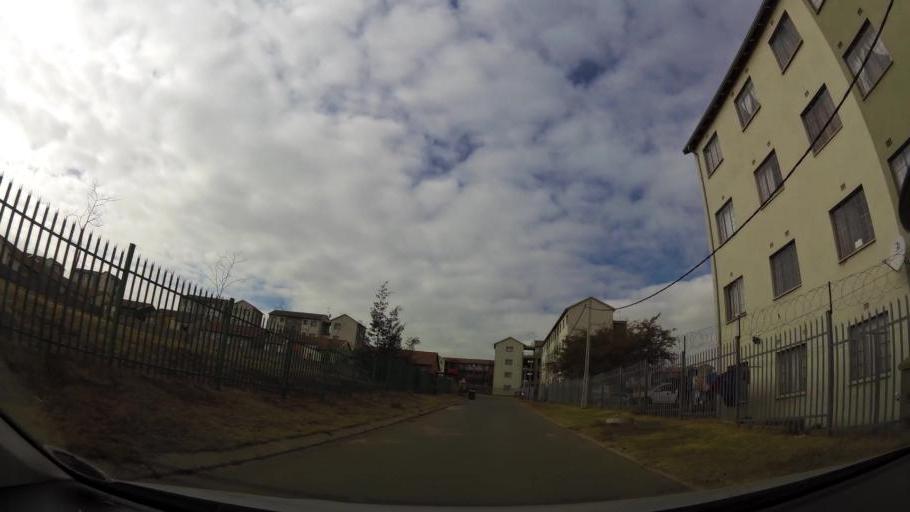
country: ZA
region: Gauteng
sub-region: City of Johannesburg Metropolitan Municipality
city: Roodepoort
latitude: -26.1906
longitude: 27.9072
